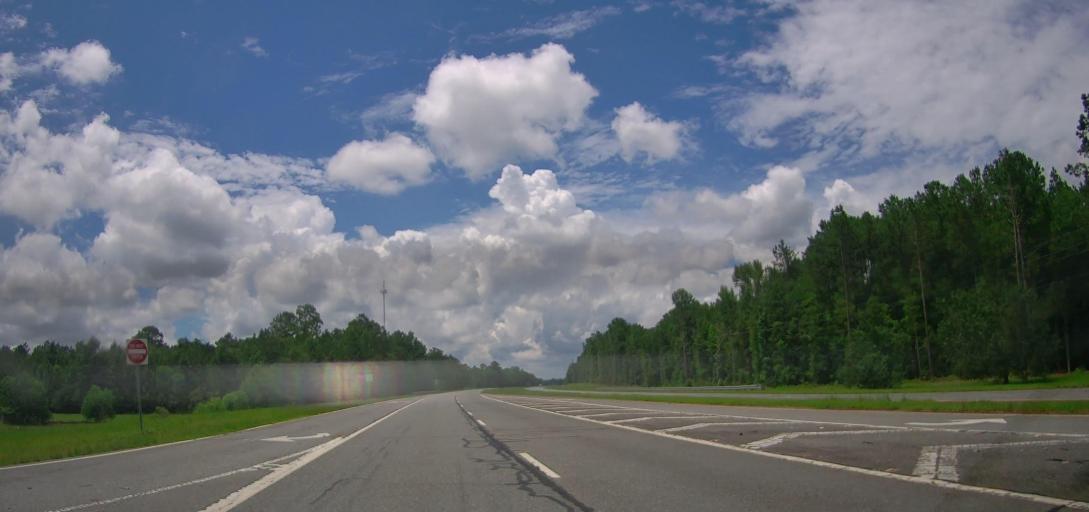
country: US
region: Georgia
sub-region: Dodge County
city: Eastman
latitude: 32.1858
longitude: -83.2000
